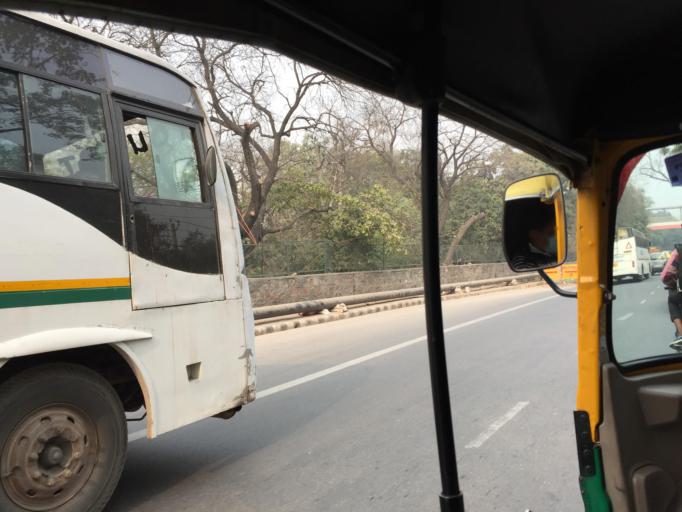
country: IN
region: NCT
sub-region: New Delhi
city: New Delhi
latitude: 28.5129
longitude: 77.1851
